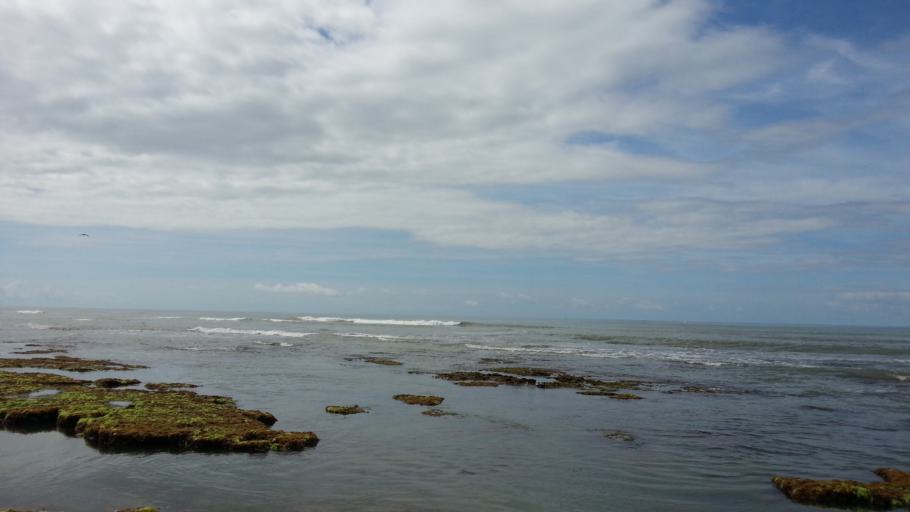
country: FR
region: Poitou-Charentes
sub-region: Departement de la Charente-Maritime
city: Dolus-d'Oleron
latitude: 45.9026
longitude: -1.3141
